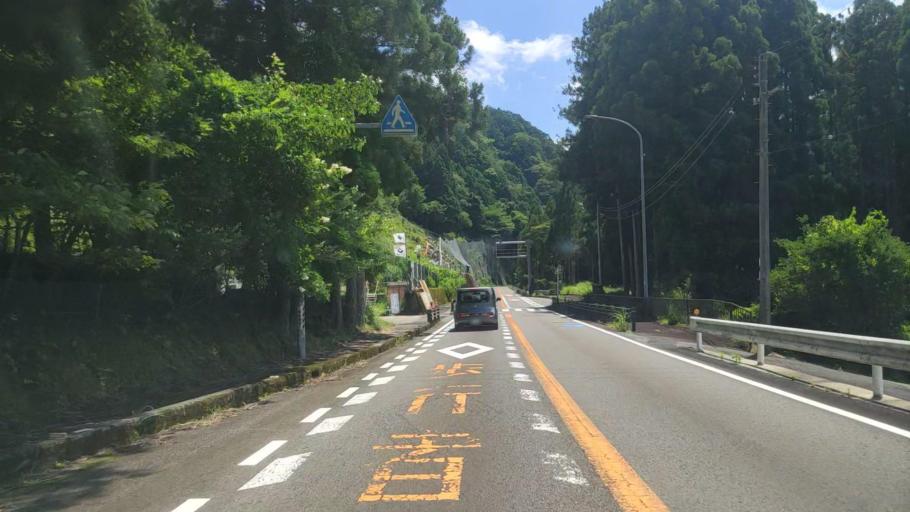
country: JP
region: Mie
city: Owase
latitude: 33.9830
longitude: 136.1080
